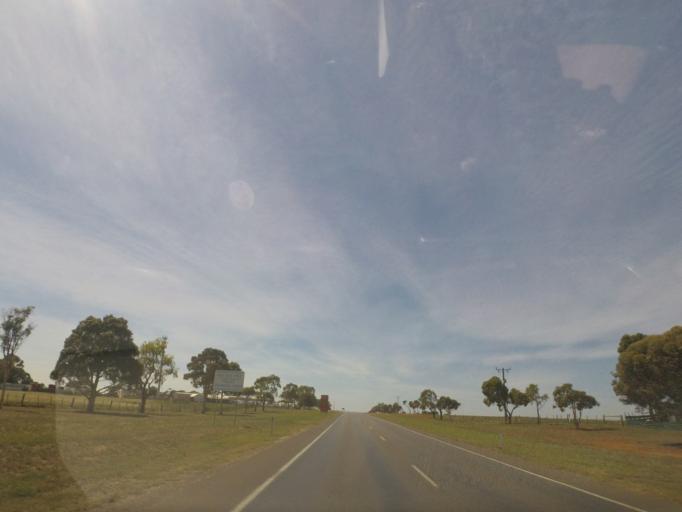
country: AU
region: Victoria
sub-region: Moorabool
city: Bacchus Marsh
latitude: -37.6923
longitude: 144.4420
